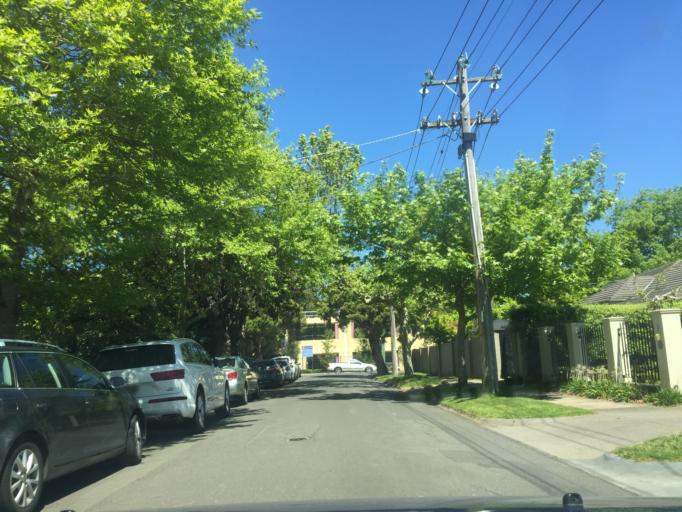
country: AU
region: Victoria
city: Balwyn
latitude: -37.8193
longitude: 145.0702
